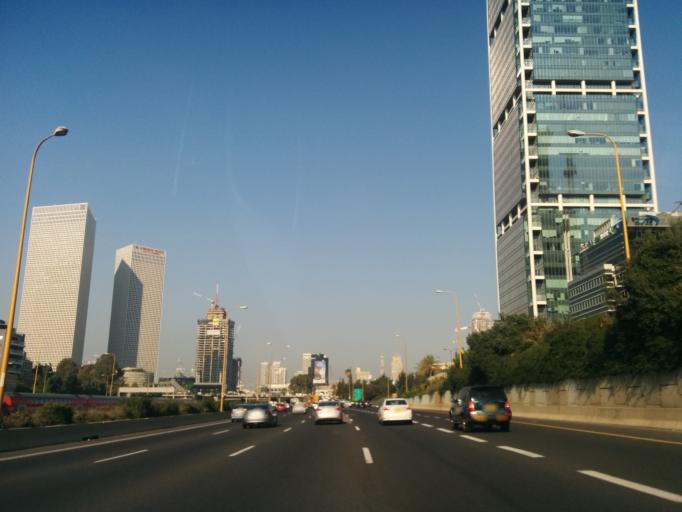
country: IL
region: Tel Aviv
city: Tel Aviv
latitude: 32.0685
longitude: 34.7930
